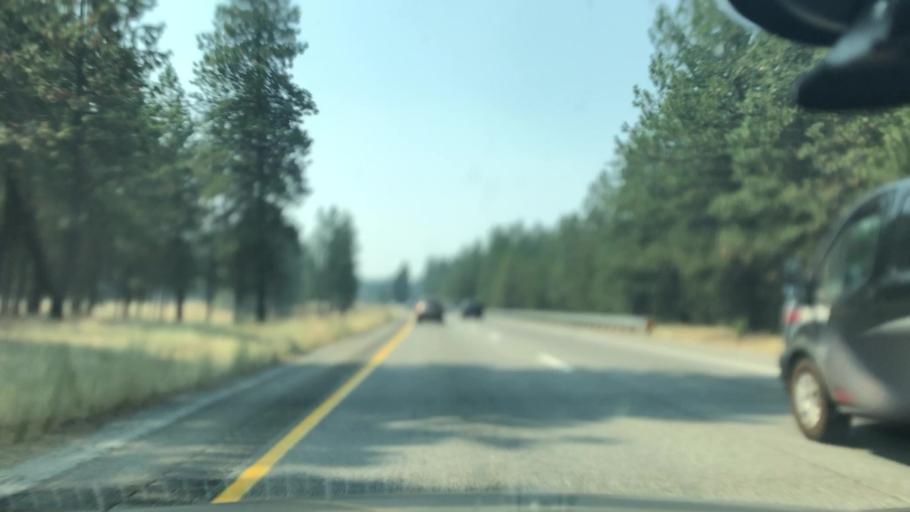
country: US
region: Idaho
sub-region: Kootenai County
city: Coeur d'Alene
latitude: 47.7090
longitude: -116.8580
